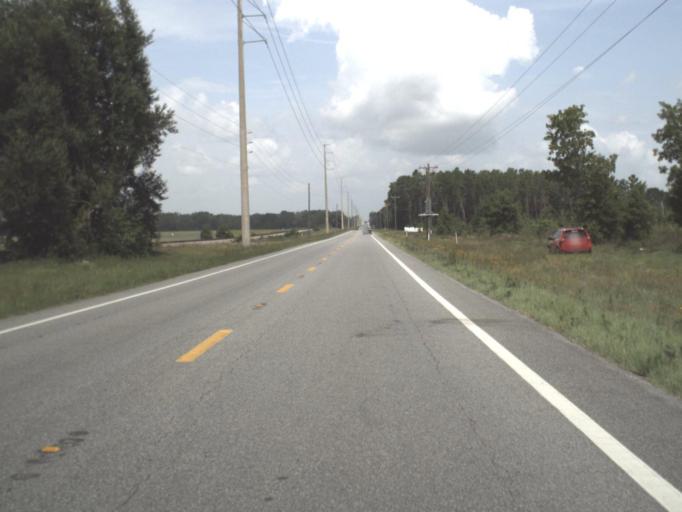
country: US
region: Florida
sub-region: Madison County
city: Madison
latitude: 30.4046
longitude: -83.2374
